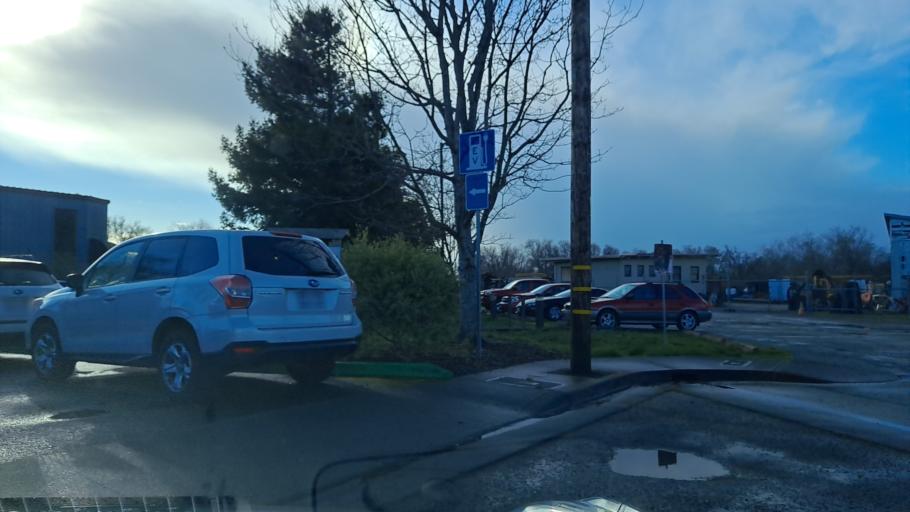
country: US
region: California
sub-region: Humboldt County
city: Arcata
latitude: 40.8696
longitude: -124.0933
